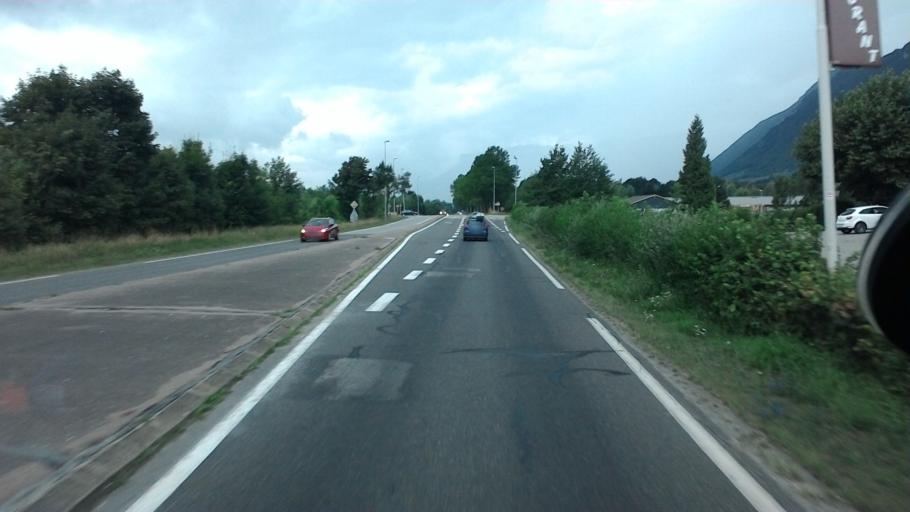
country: FR
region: Rhone-Alpes
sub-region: Departement de la Savoie
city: Coise-Saint-Jean-Pied-Gauthier
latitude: 45.5309
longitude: 6.1194
